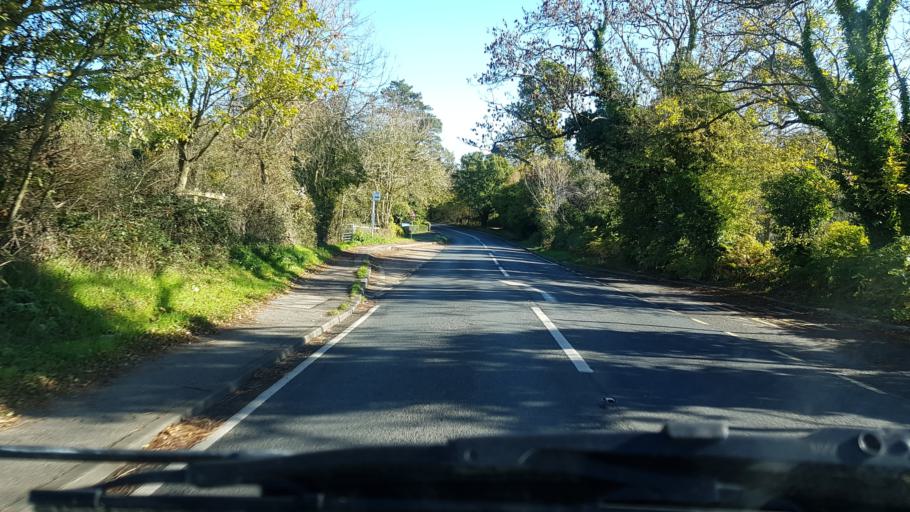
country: GB
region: England
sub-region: Surrey
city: Dorking
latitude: 51.2268
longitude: -0.3537
